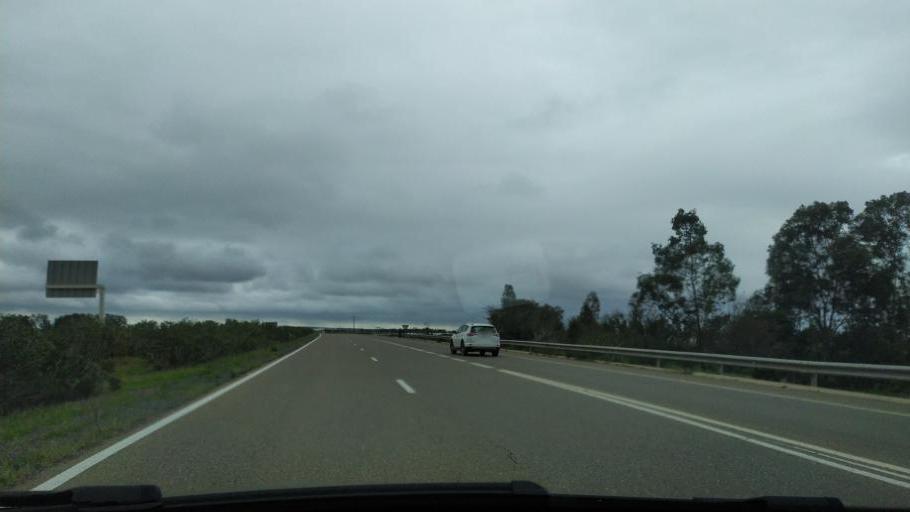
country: MA
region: Gharb-Chrarda-Beni Hssen
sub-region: Kenitra Province
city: Lalla Mimouna
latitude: 34.8590
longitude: -6.2224
